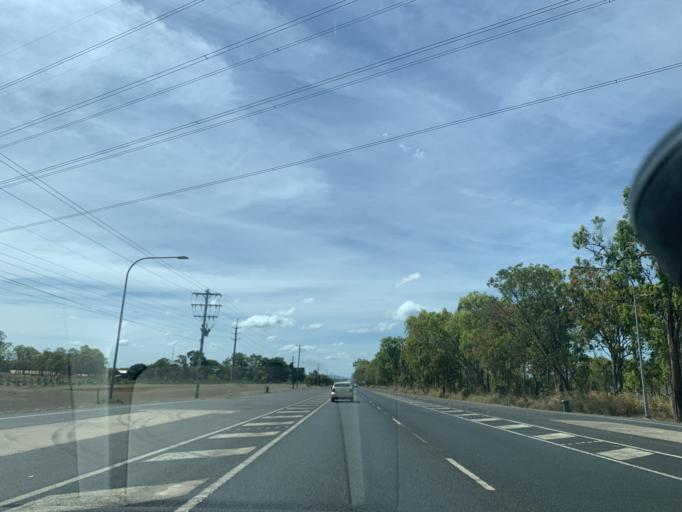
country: AU
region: Queensland
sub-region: Tablelands
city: Tolga
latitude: -17.1369
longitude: 145.4303
